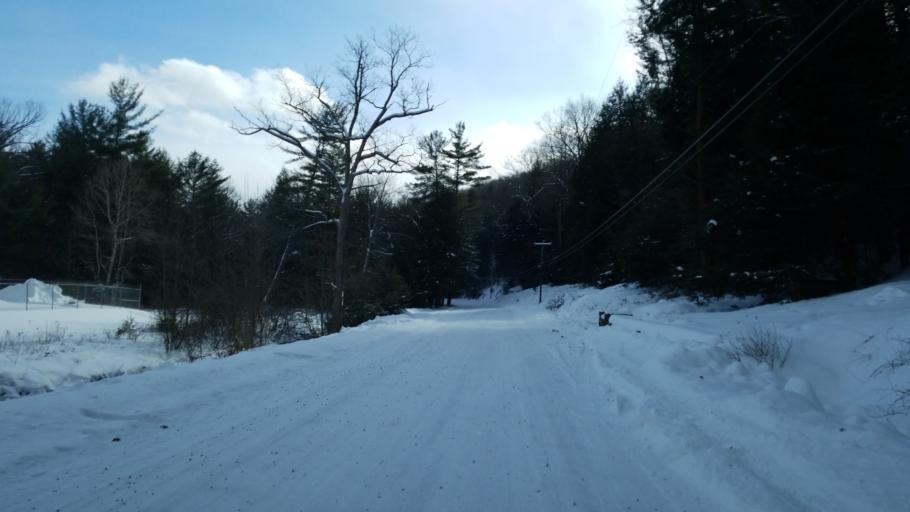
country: US
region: Pennsylvania
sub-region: Clearfield County
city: Clearfield
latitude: 41.0523
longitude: -78.4725
